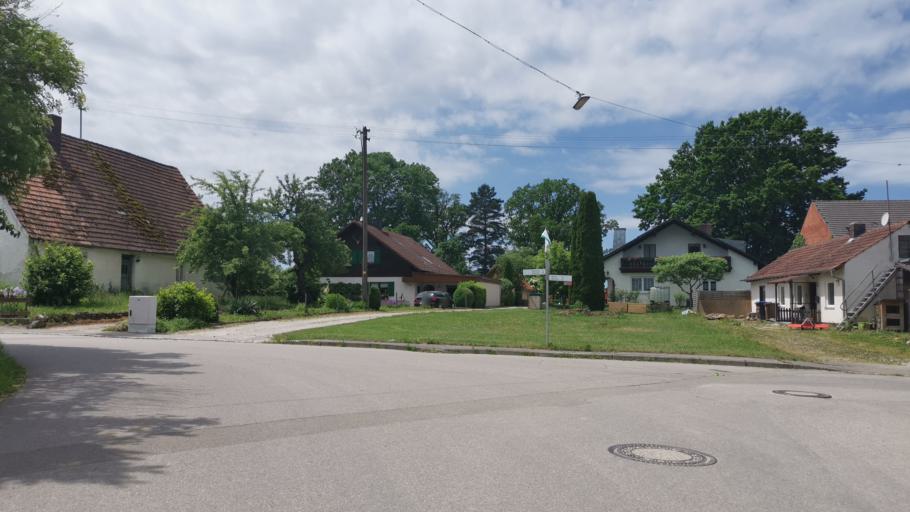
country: DE
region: Bavaria
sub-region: Swabia
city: Steindorf
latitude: 48.2384
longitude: 11.0175
